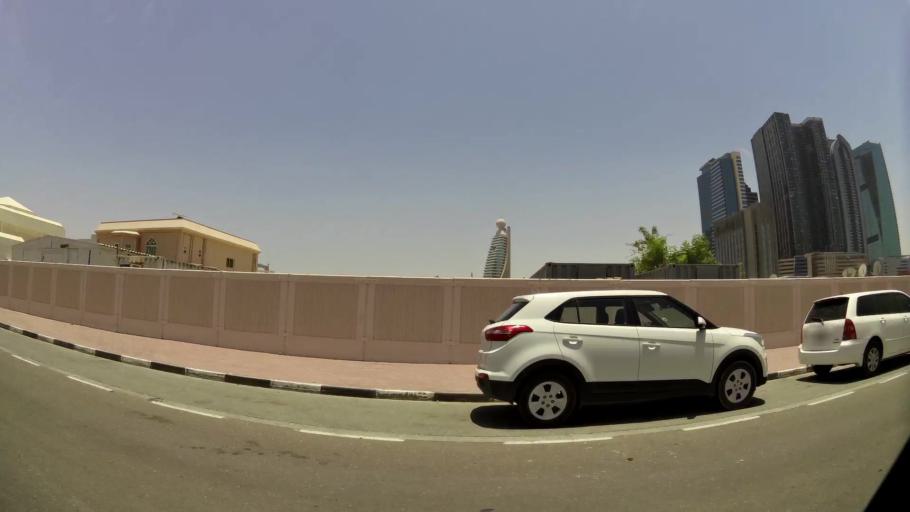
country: AE
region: Ash Shariqah
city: Sharjah
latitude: 25.2339
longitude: 55.2841
